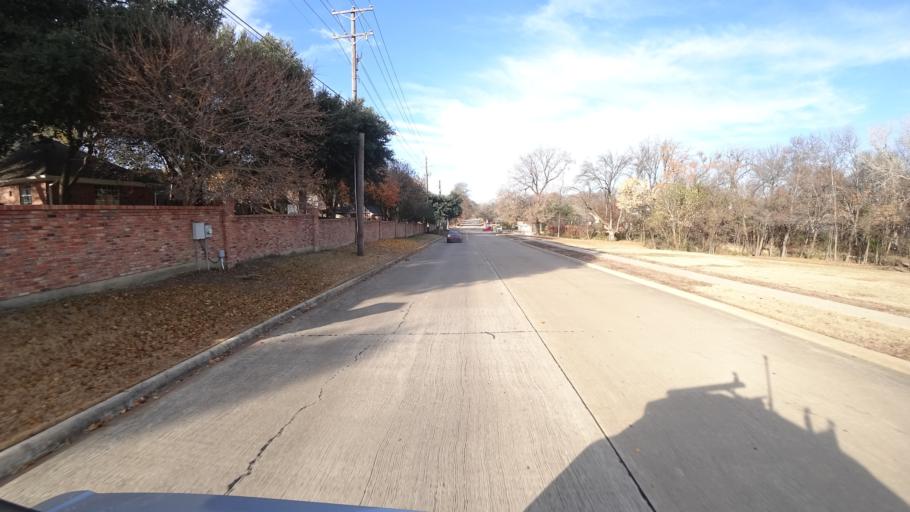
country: US
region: Texas
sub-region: Collin County
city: McKinney
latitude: 33.2047
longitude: -96.6532
